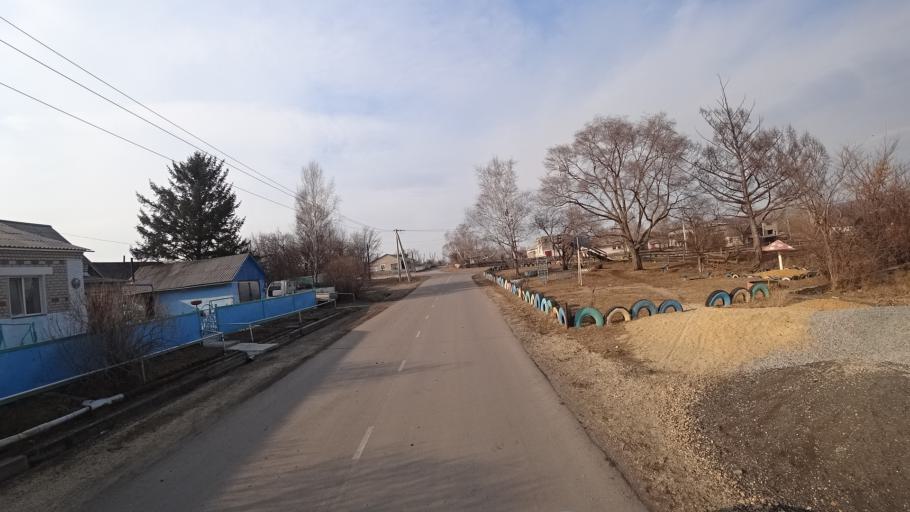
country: RU
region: Amur
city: Novobureyskiy
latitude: 49.8989
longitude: 129.8774
